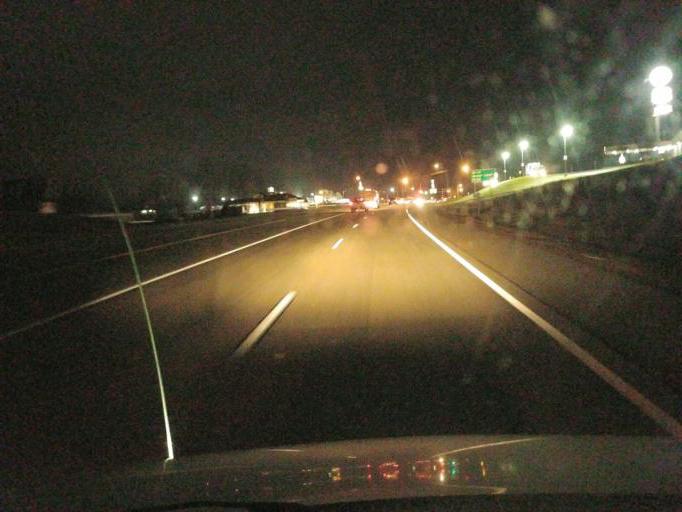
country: US
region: Missouri
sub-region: Franklin County
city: Villa Ridge
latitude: 38.4757
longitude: -90.8558
